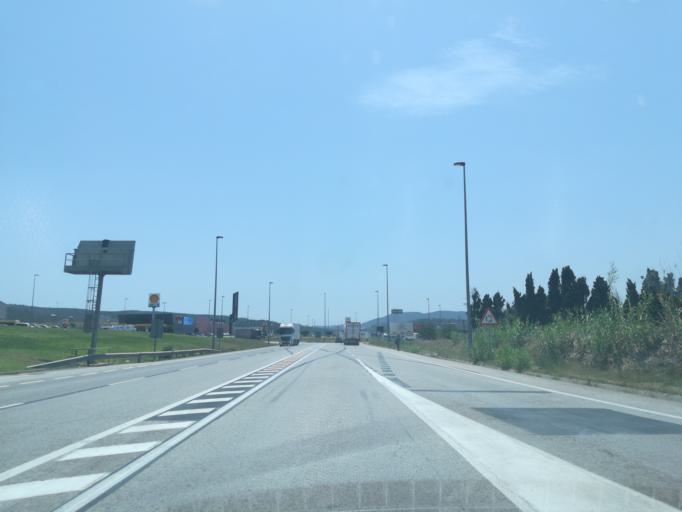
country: ES
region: Catalonia
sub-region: Provincia de Girona
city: la Jonquera
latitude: 42.4061
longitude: 2.8781
